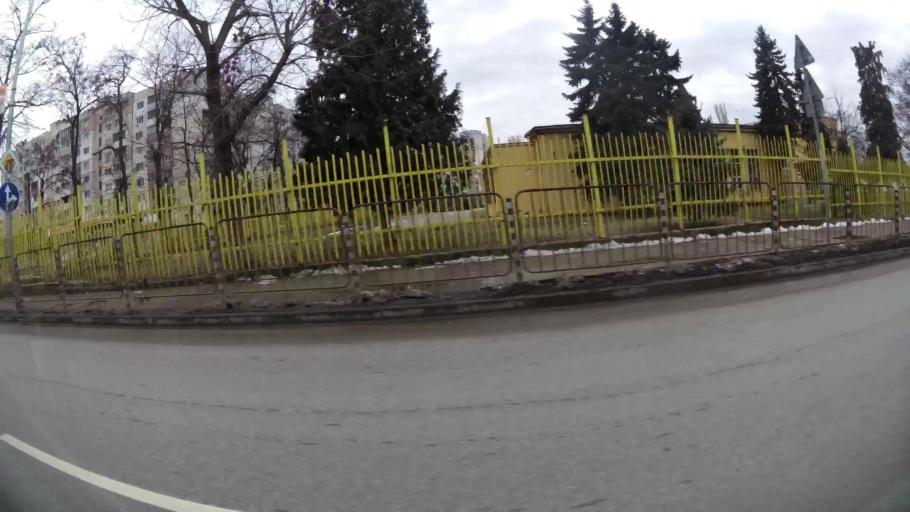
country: BG
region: Sofia-Capital
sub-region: Stolichna Obshtina
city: Sofia
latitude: 42.7389
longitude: 23.2888
